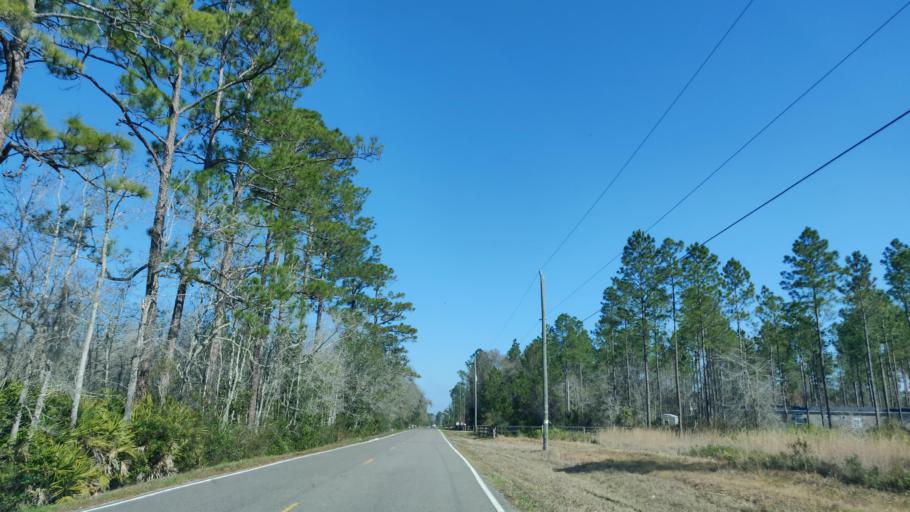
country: US
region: Florida
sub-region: Duval County
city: Baldwin
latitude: 30.1955
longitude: -81.9660
